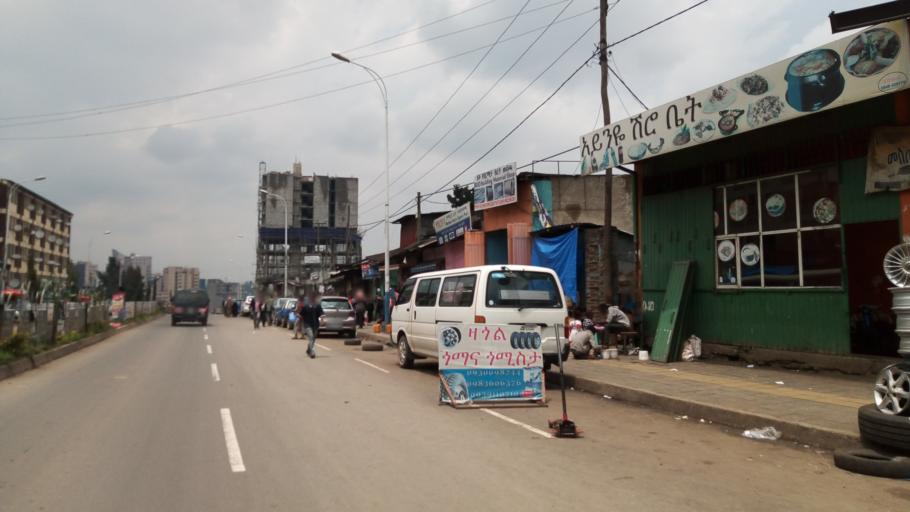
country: ET
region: Adis Abeba
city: Addis Ababa
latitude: 9.0285
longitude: 38.7449
